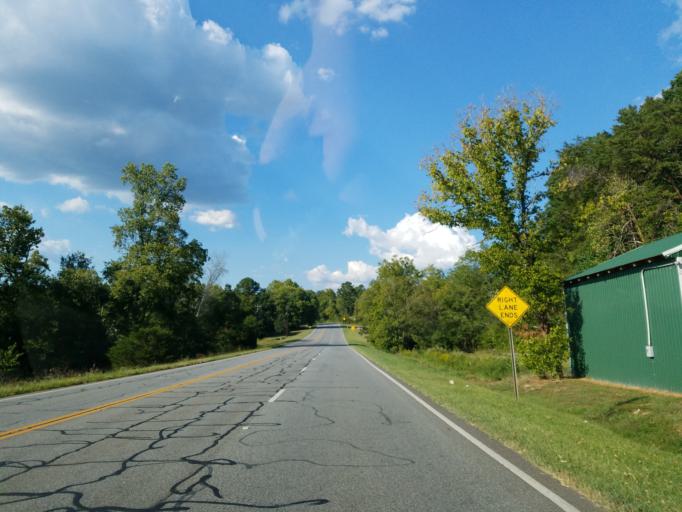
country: US
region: Georgia
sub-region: Bartow County
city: Rydal
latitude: 34.4847
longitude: -84.7065
